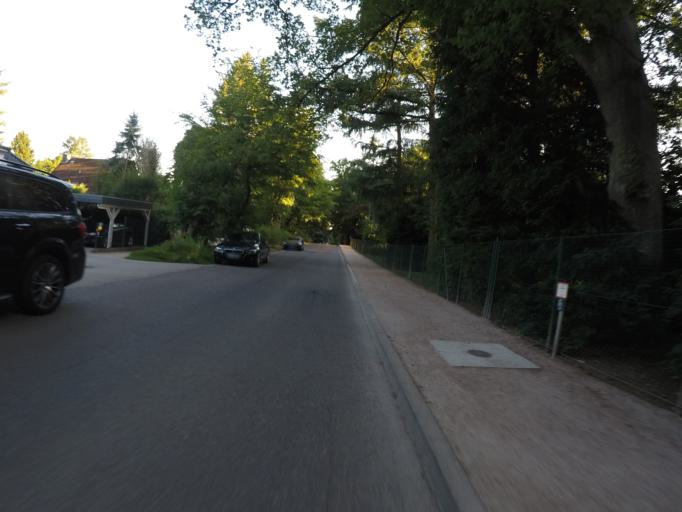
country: DE
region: Hamburg
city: Poppenbuettel
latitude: 53.6649
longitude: 10.0985
